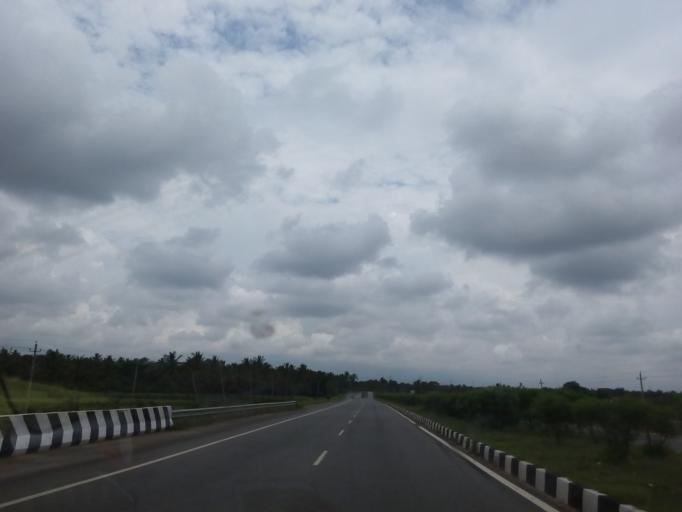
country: IN
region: Karnataka
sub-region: Hassan
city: Hassan
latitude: 12.9771
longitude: 76.2422
